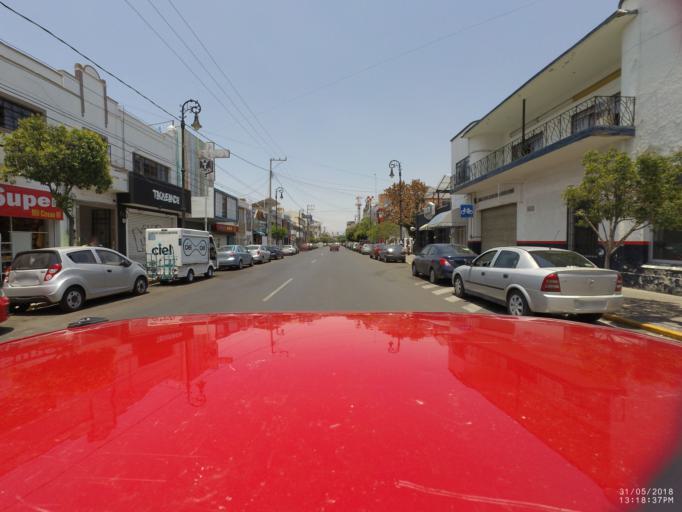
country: MX
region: Aguascalientes
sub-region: Aguascalientes
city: Aguascalientes
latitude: 21.8835
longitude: -102.2878
